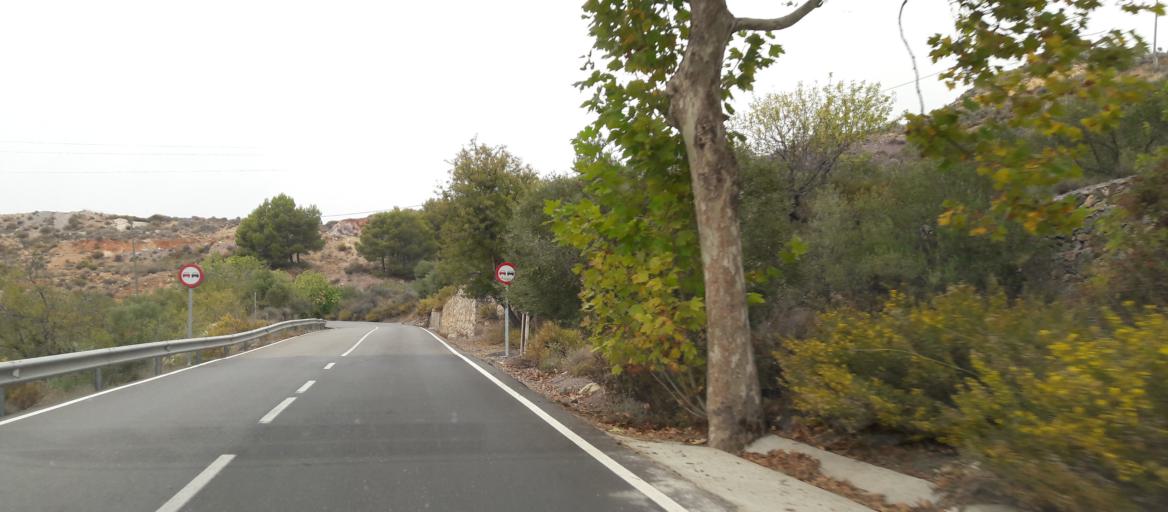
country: ES
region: Andalusia
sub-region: Provincia de Almeria
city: Enix
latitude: 36.8752
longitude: -2.6186
